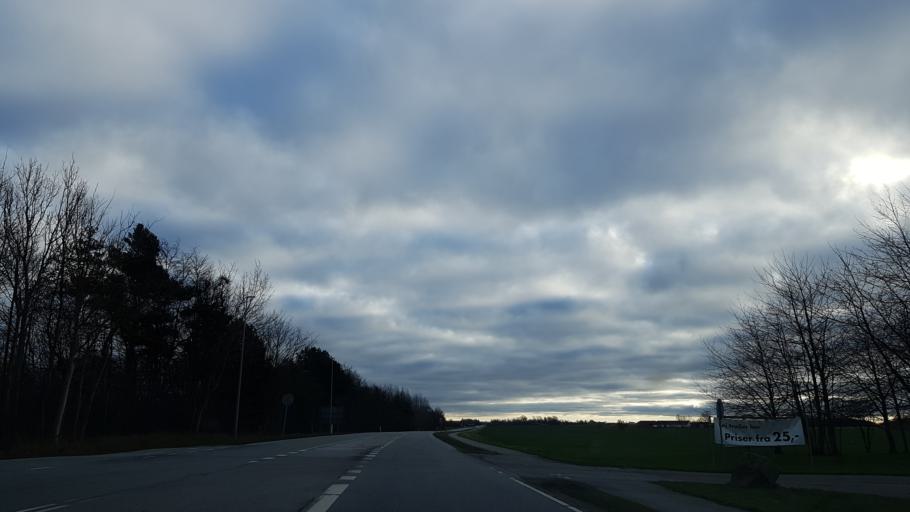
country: DK
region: Zealand
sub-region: Kalundborg Kommune
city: Gorlev
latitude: 55.5343
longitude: 11.2239
